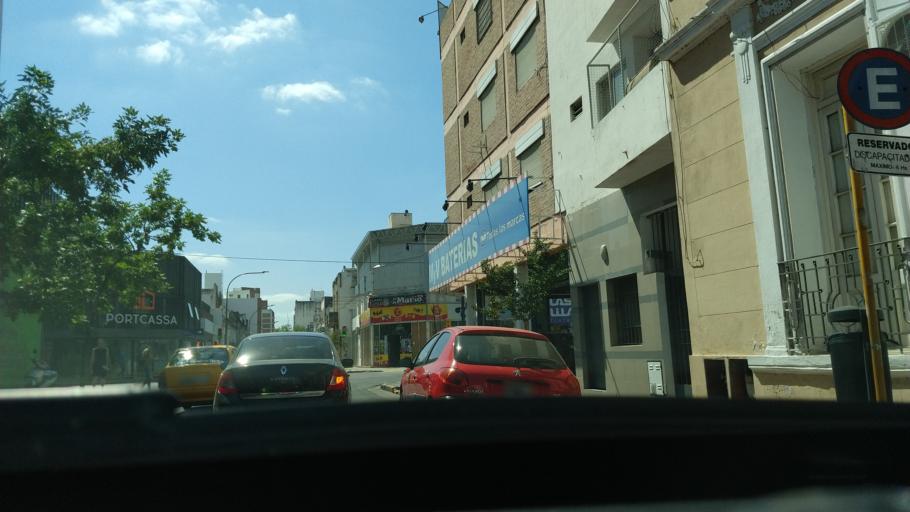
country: AR
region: Cordoba
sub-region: Departamento de Capital
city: Cordoba
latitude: -31.4077
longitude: -64.1949
